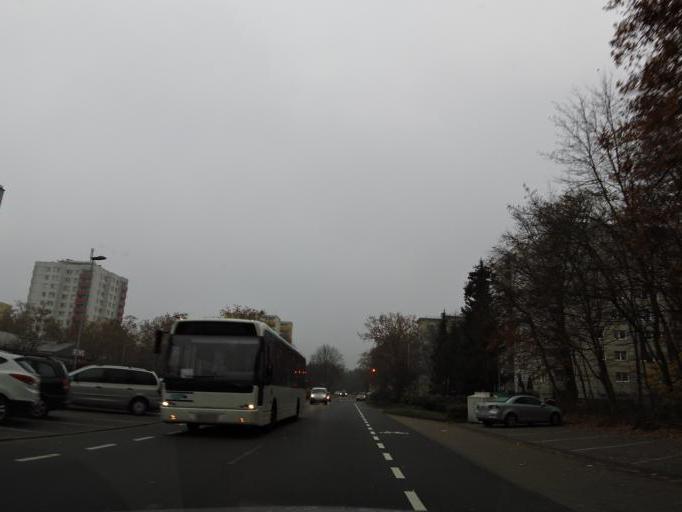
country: DE
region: Hesse
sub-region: Regierungsbezirk Darmstadt
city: Neu Isenburg
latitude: 50.0522
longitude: 8.6700
